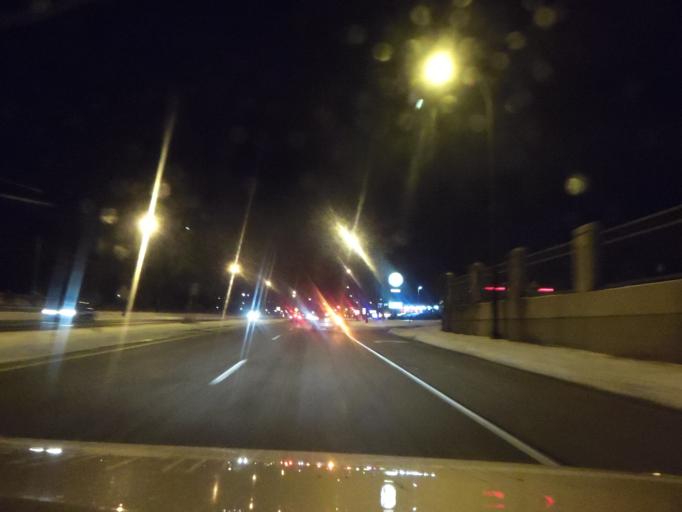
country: US
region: Minnesota
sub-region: Hennepin County
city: Richfield
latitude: 44.9179
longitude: -93.2169
